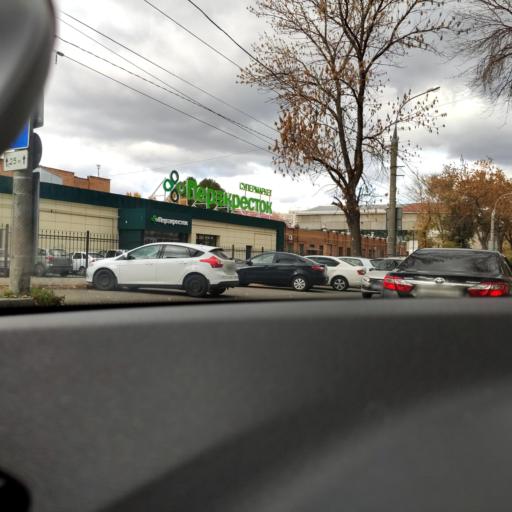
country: RU
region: Samara
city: Samara
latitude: 53.2026
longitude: 50.1328
